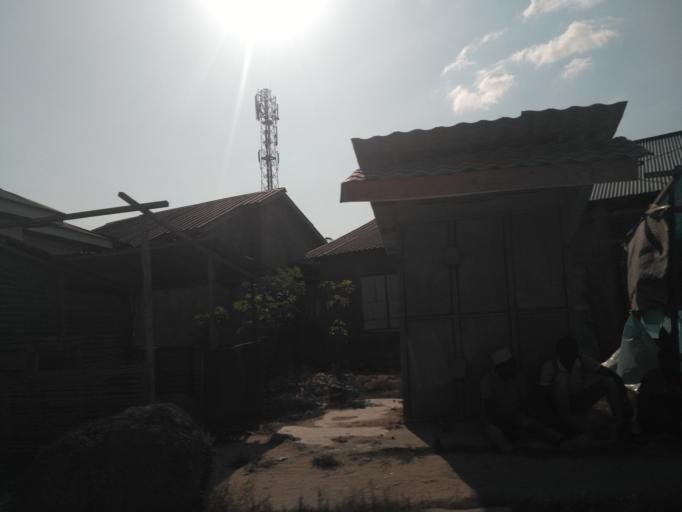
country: TZ
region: Dar es Salaam
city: Dar es Salaam
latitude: -6.8650
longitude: 39.3111
